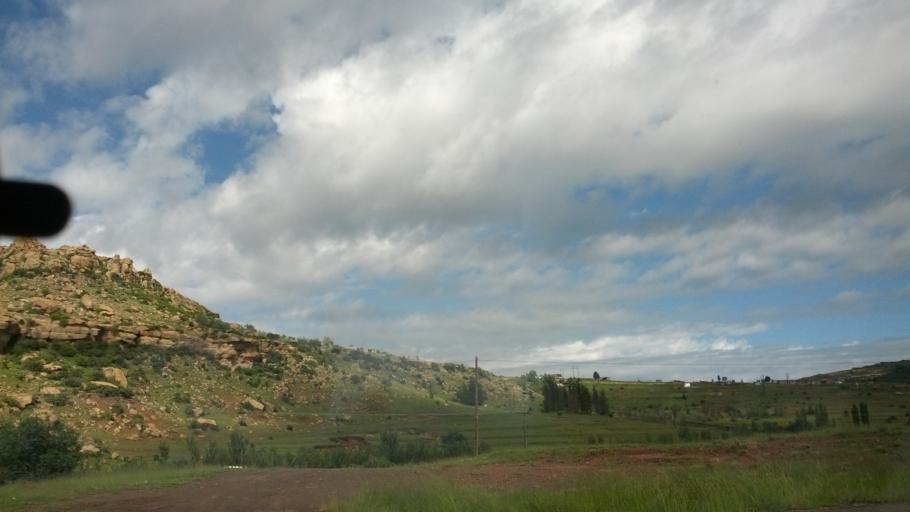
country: LS
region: Berea
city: Teyateyaneng
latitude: -29.1432
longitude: 27.7138
